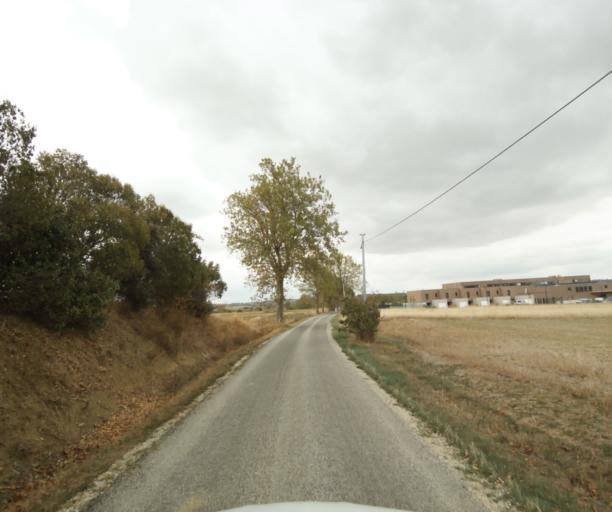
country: FR
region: Midi-Pyrenees
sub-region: Departement de la Haute-Garonne
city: Villefranche-de-Lauragais
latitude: 43.3999
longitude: 1.7289
